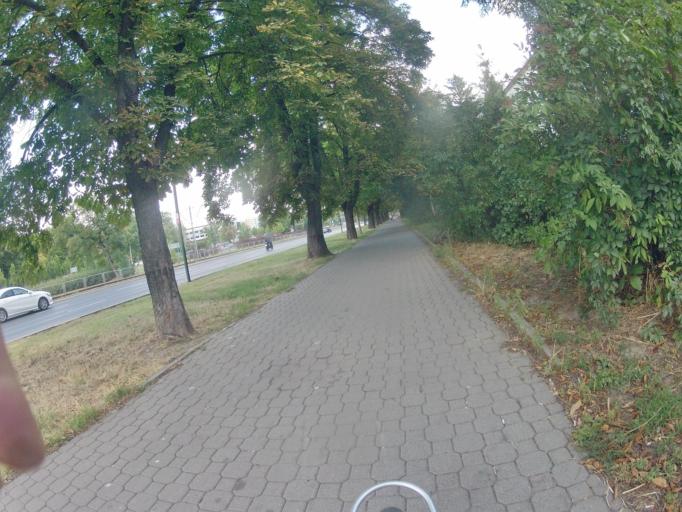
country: PL
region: Masovian Voivodeship
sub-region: Warszawa
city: Ochota
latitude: 52.1974
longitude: 21.0020
